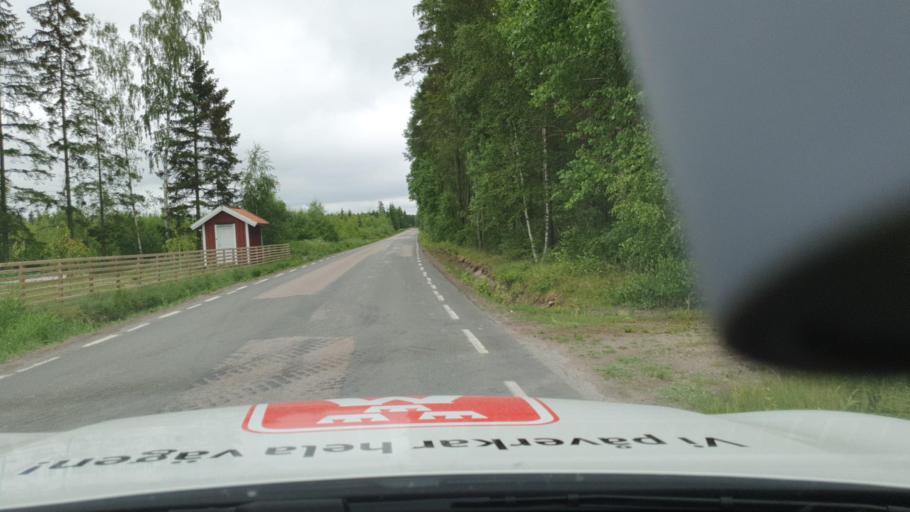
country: SE
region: Vaestra Goetaland
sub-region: Tibro Kommun
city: Tibro
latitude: 58.3863
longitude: 14.0593
